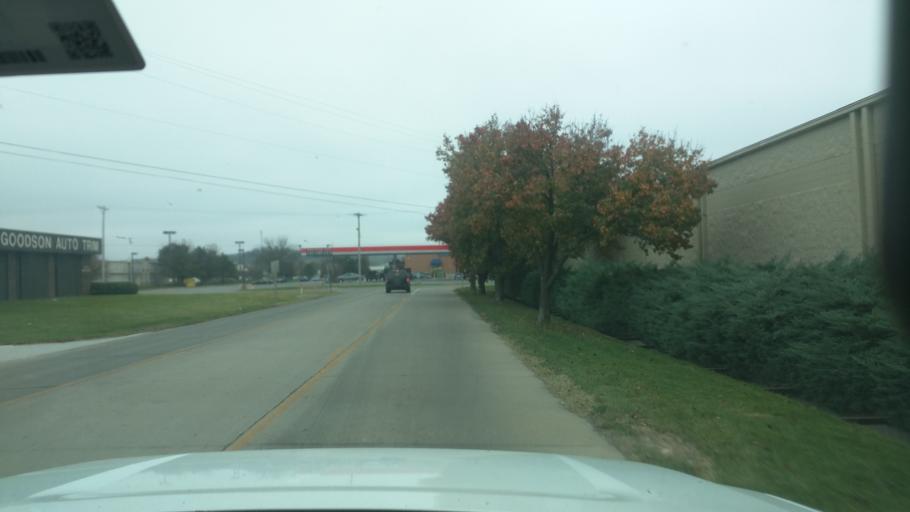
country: US
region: Kansas
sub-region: Riley County
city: Manhattan
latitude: 39.1847
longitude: -96.5557
